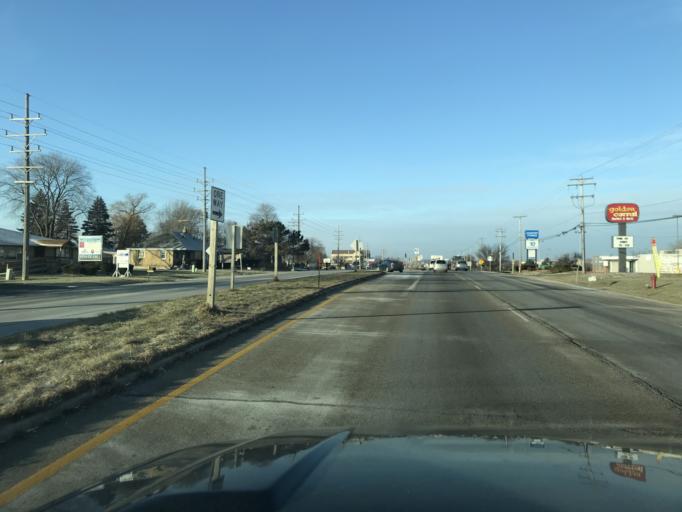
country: US
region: Wisconsin
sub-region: Kenosha County
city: Pleasant Prairie
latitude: 42.5667
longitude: -87.8821
